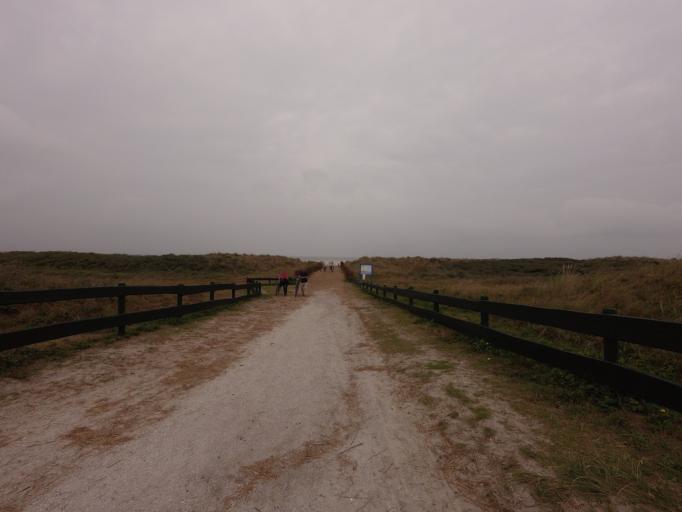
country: NL
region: Friesland
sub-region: Gemeente Schiermonnikoog
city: Schiermonnikoog
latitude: 53.4977
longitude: 6.1887
